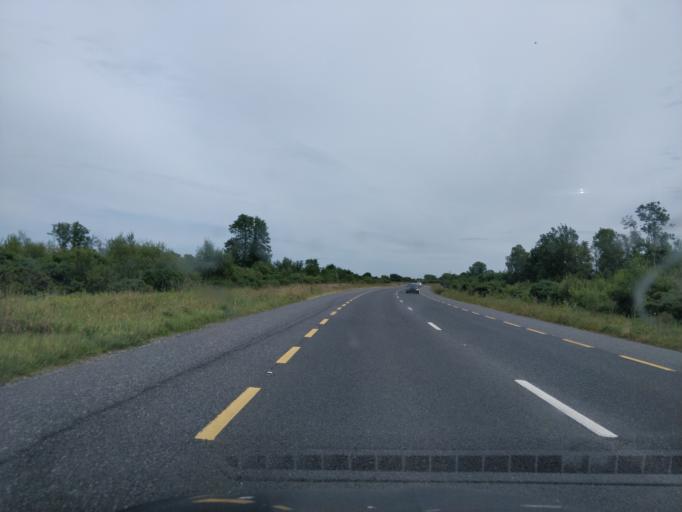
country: IE
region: Leinster
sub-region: Uibh Fhaili
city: Tullamore
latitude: 53.2523
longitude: -7.4965
